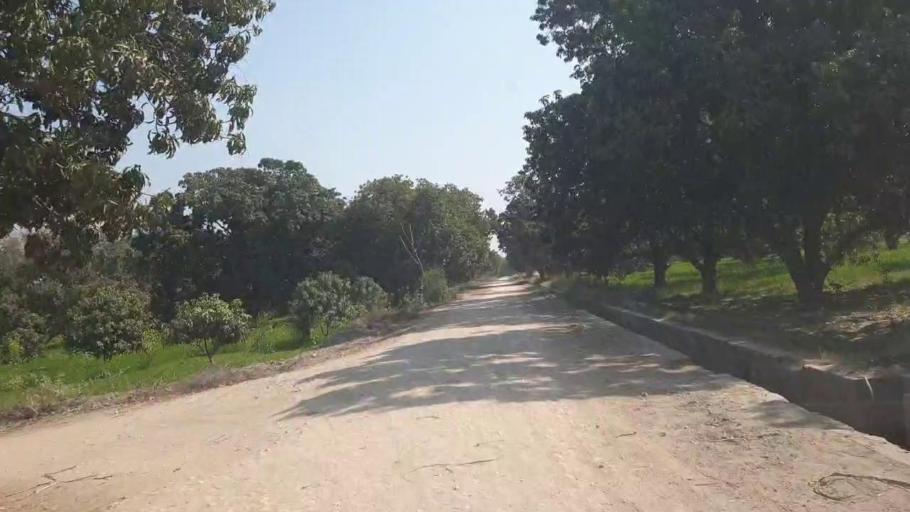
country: PK
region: Sindh
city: Tando Allahyar
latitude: 25.4336
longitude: 68.8478
